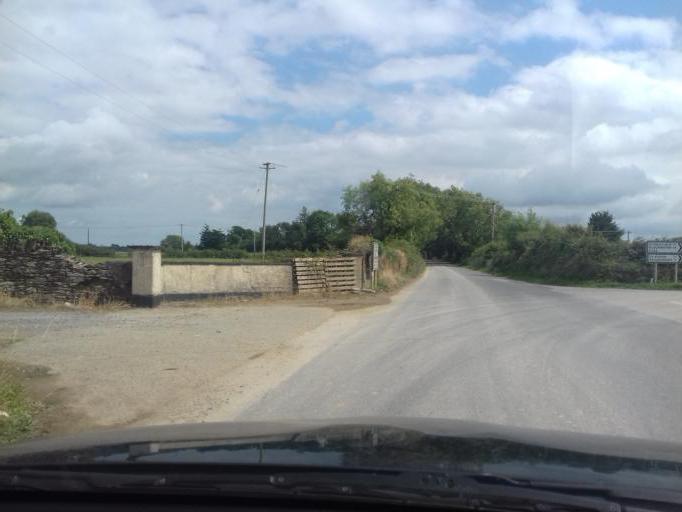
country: IE
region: Leinster
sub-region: Loch Garman
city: Enniscorthy
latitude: 52.5015
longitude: -6.5192
